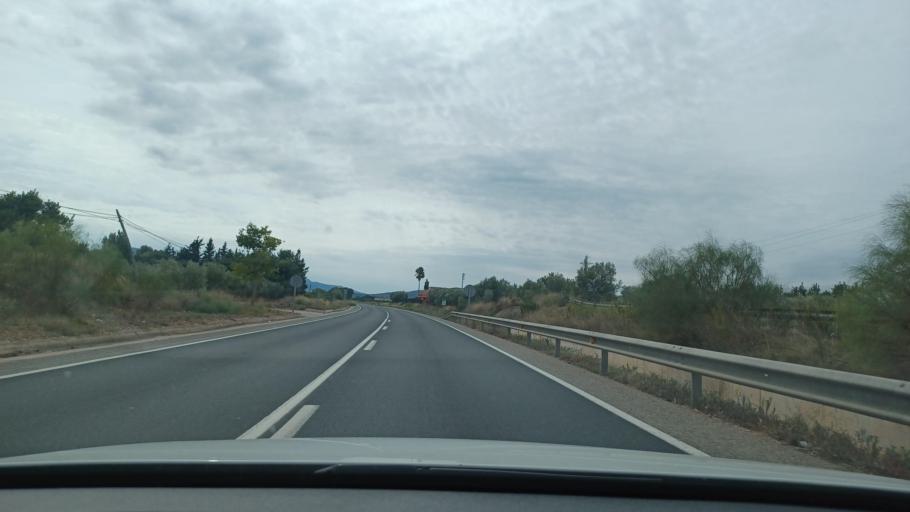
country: ES
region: Catalonia
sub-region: Provincia de Tarragona
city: Santa Barbara
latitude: 40.7350
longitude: 0.5031
